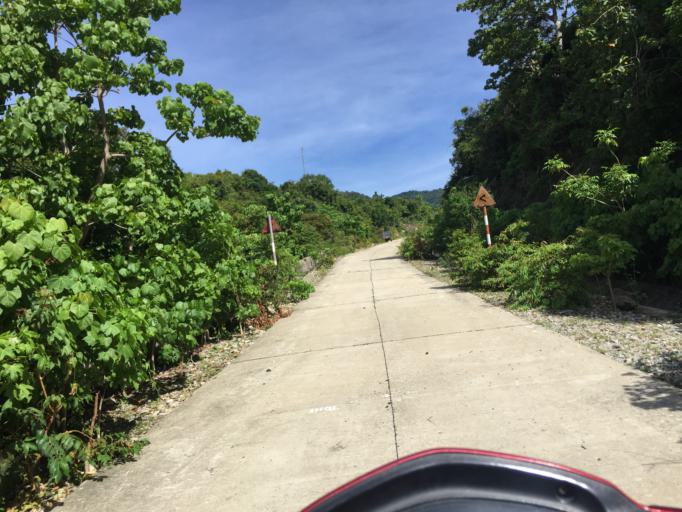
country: VN
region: Quang Nam
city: Hoi An
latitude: 15.9348
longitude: 108.5311
